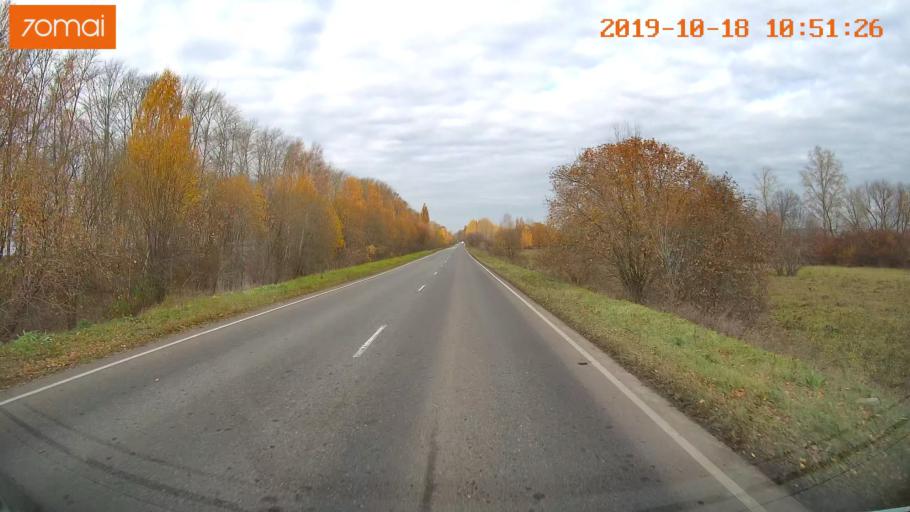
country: RU
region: Tula
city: Yepifan'
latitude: 53.7545
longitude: 38.6680
